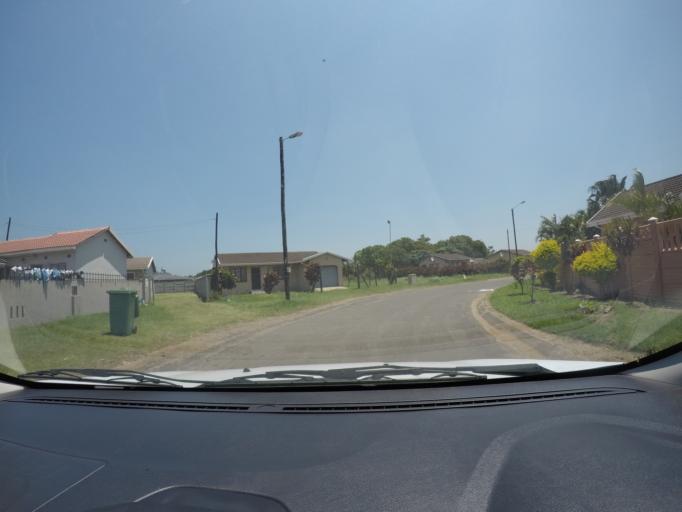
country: ZA
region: KwaZulu-Natal
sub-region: uThungulu District Municipality
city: eSikhawini
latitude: -28.8885
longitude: 31.8895
